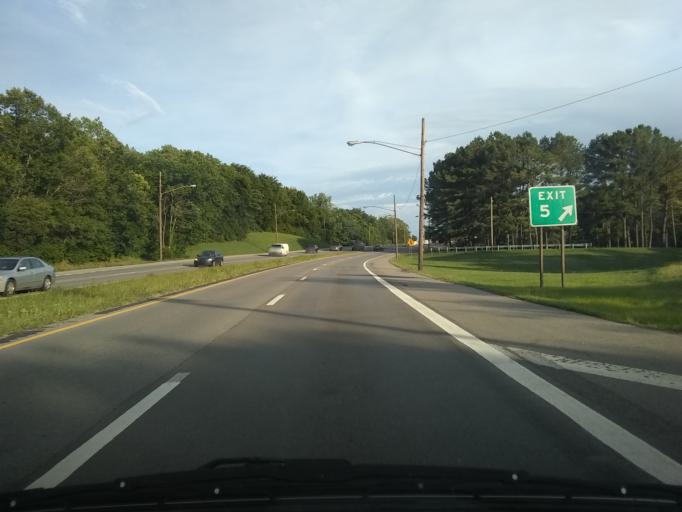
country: US
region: Tennessee
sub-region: Davidson County
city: Nashville
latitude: 36.1325
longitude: -86.6961
